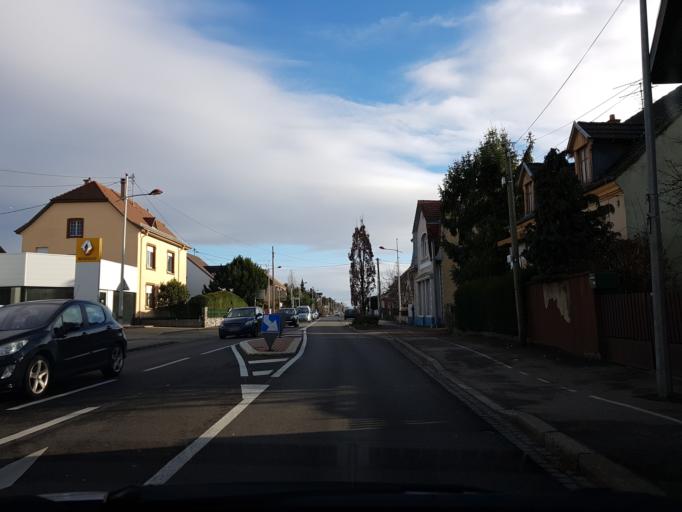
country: FR
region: Alsace
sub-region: Departement du Haut-Rhin
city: Rixheim
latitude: 47.7496
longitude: 7.4082
